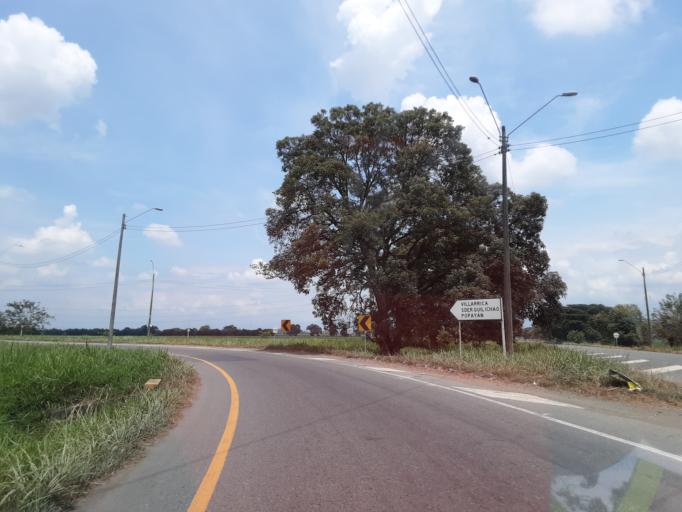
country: CO
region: Cauca
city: Puerto Tejada
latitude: 3.2337
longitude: -76.3949
